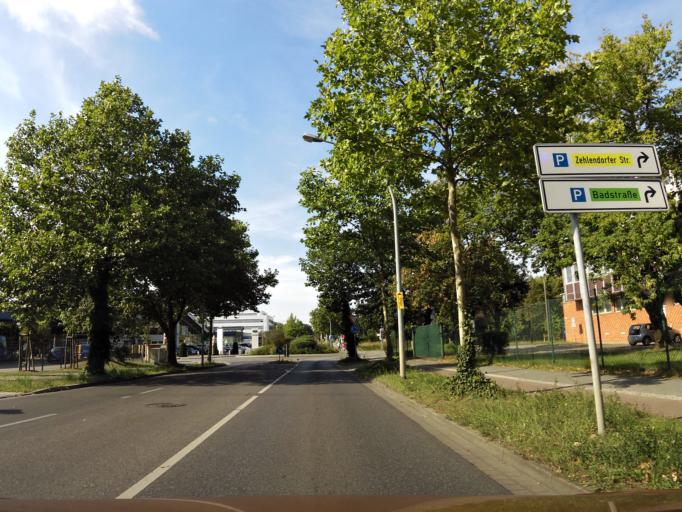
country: DE
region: Brandenburg
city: Teltow
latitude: 52.3988
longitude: 13.2420
